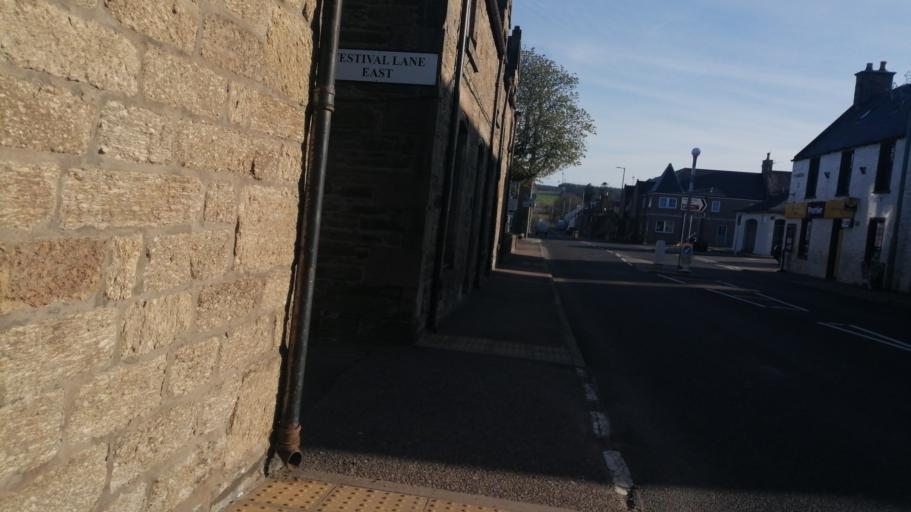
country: GB
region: Scotland
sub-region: Moray
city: Keith
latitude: 57.5389
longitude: -2.9486
